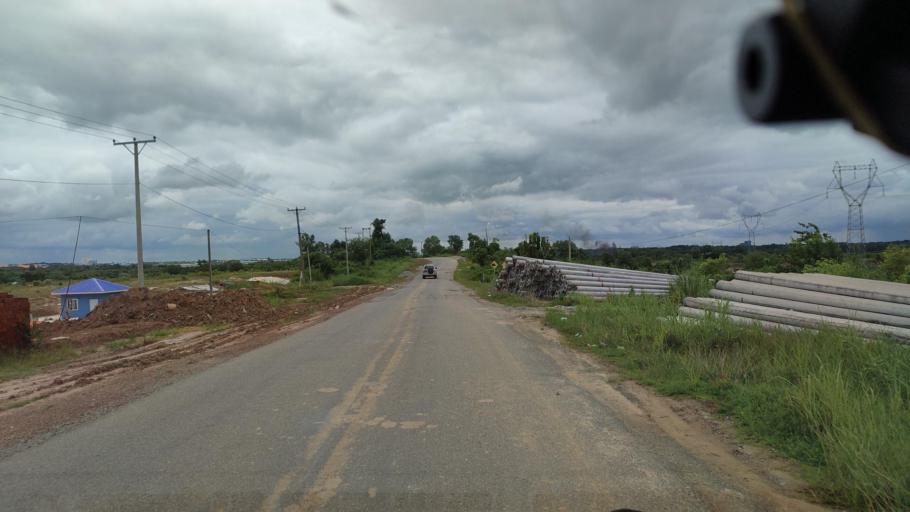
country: MM
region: Bago
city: Bago
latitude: 17.2523
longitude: 96.4306
